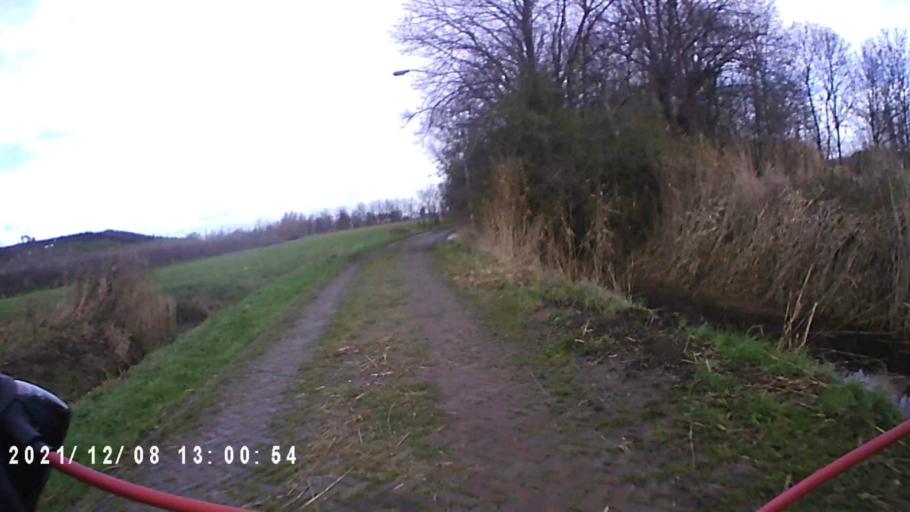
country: NL
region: Groningen
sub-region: Gemeente Haren
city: Haren
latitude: 53.2018
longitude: 6.6260
